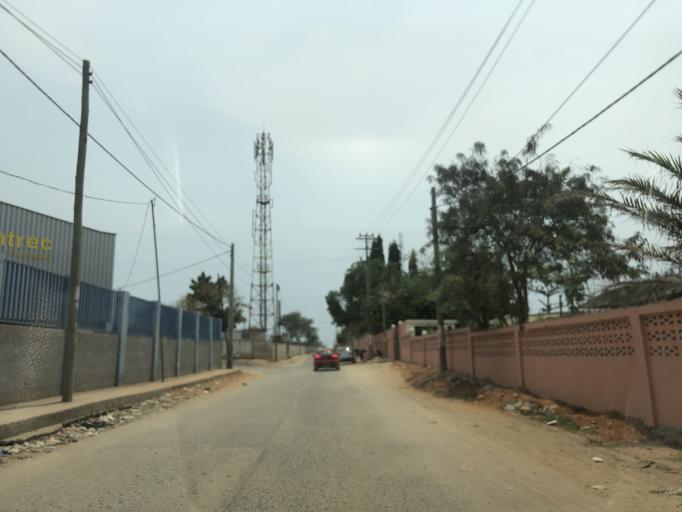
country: AO
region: Luanda
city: Luanda
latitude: -8.8893
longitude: 13.1967
